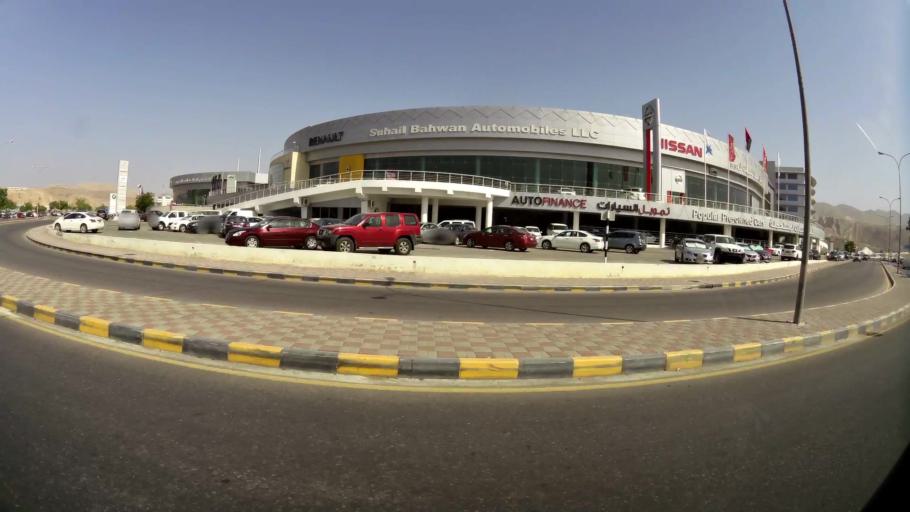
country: OM
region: Muhafazat Masqat
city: Muscat
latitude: 23.6101
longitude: 58.4925
